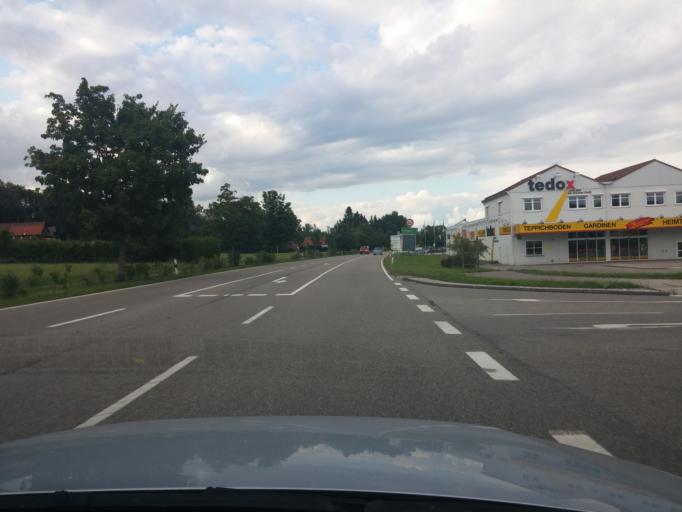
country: DE
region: Bavaria
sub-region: Swabia
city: Memmingen
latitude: 47.9673
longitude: 10.1824
